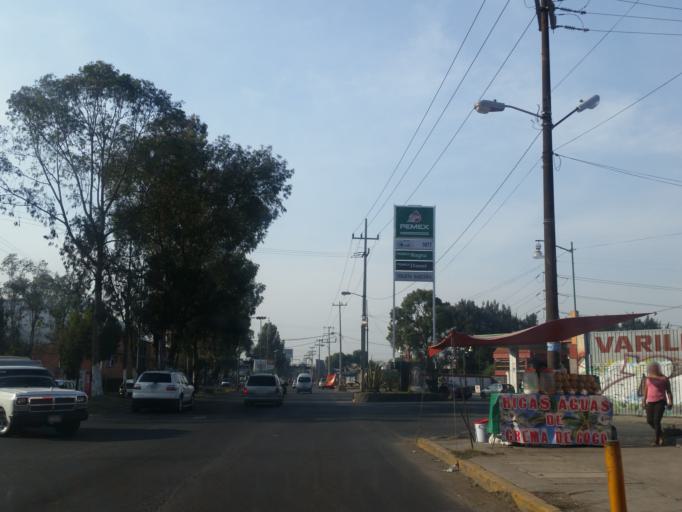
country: MX
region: Mexico
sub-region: La Paz
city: San Isidro
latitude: 19.3306
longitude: -98.9498
